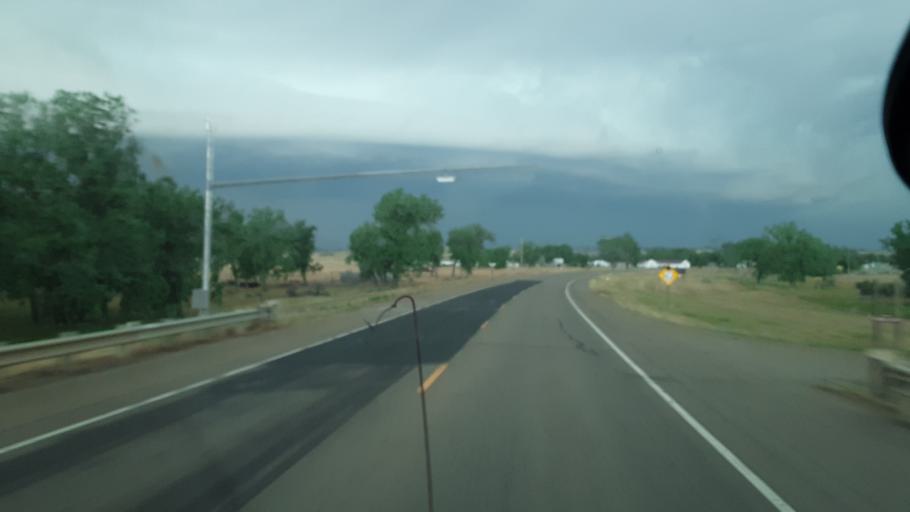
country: US
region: Montana
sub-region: Powder River County
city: Broadus
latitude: 45.4283
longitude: -105.4044
